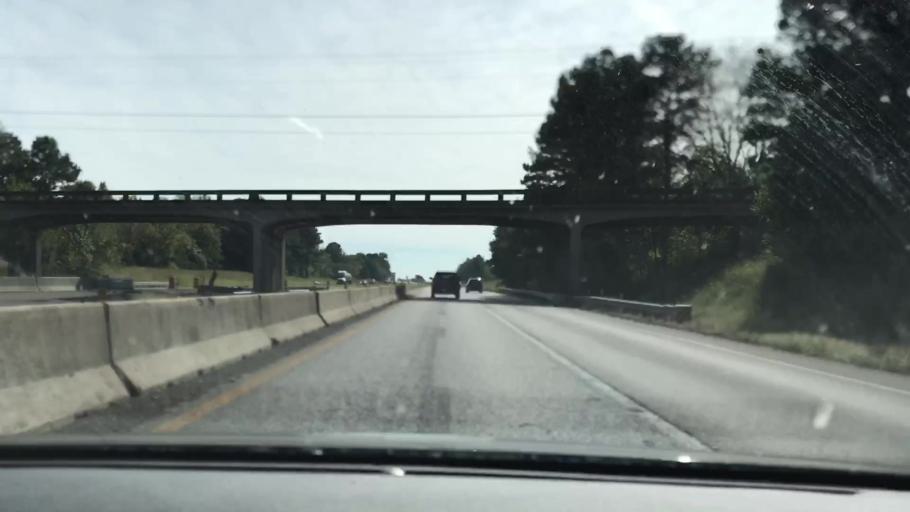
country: US
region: Tennessee
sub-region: Sumner County
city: Portland
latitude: 36.6210
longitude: -86.5770
